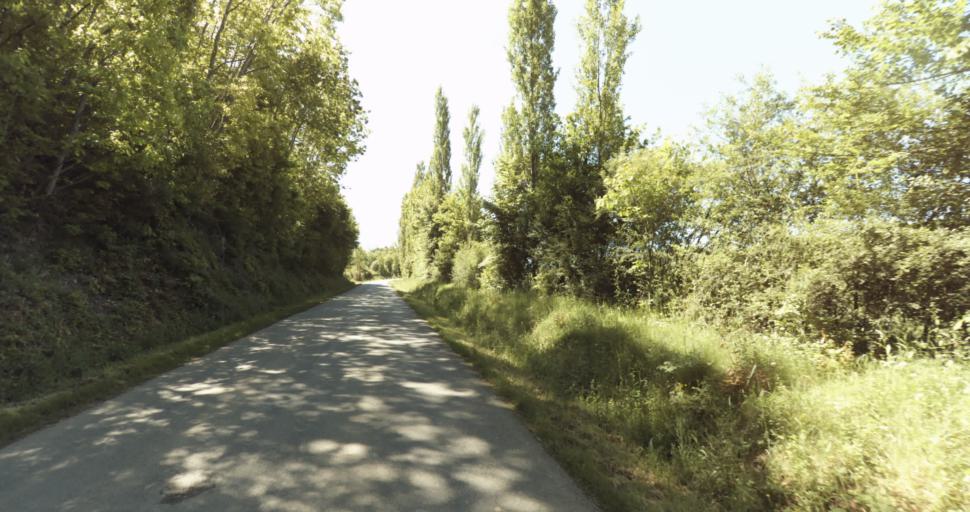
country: FR
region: Limousin
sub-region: Departement de la Haute-Vienne
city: Le Vigen
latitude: 45.7455
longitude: 1.3081
